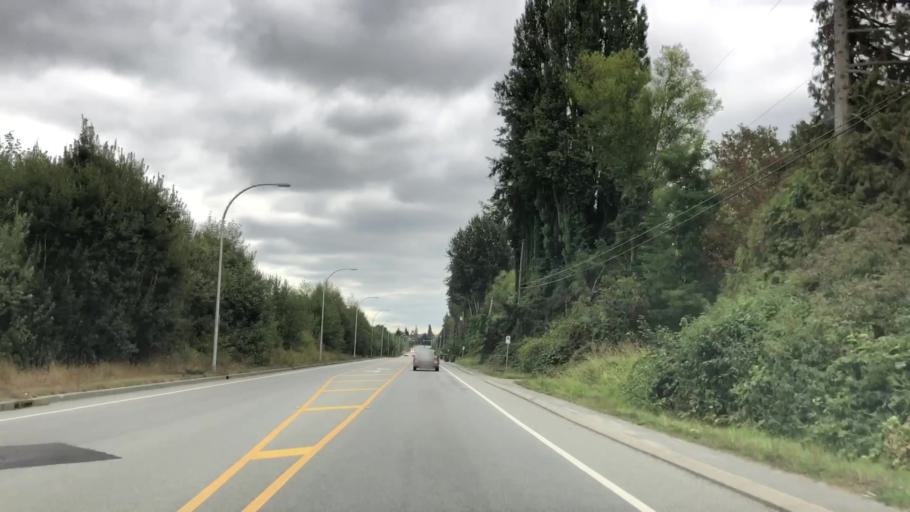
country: CA
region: British Columbia
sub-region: Greater Vancouver Regional District
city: White Rock
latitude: 49.0602
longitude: -122.7671
